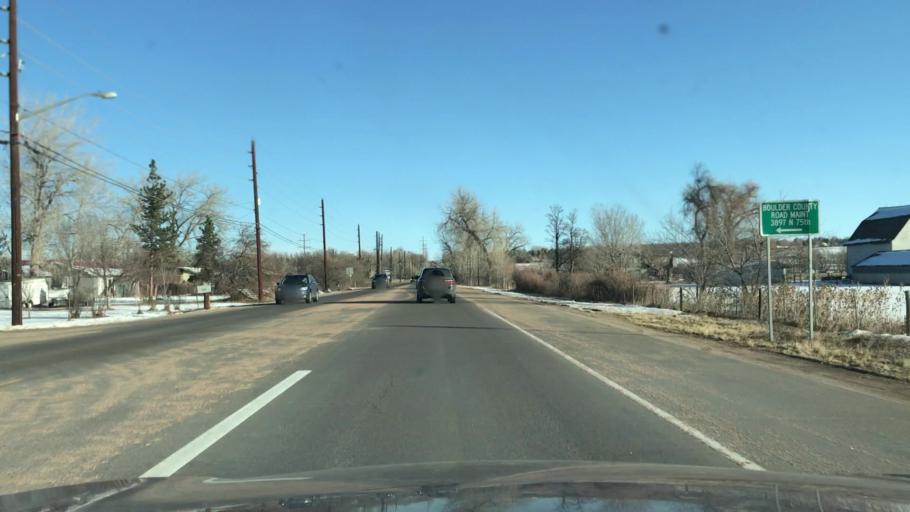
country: US
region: Colorado
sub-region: Boulder County
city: Gunbarrel
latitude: 40.0454
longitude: -105.1783
